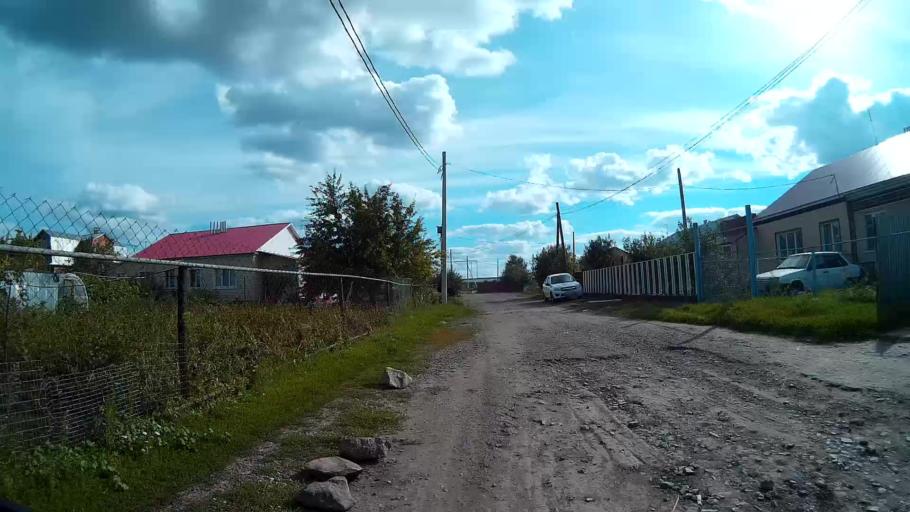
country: RU
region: Ulyanovsk
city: Isheyevka
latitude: 54.2878
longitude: 48.2124
